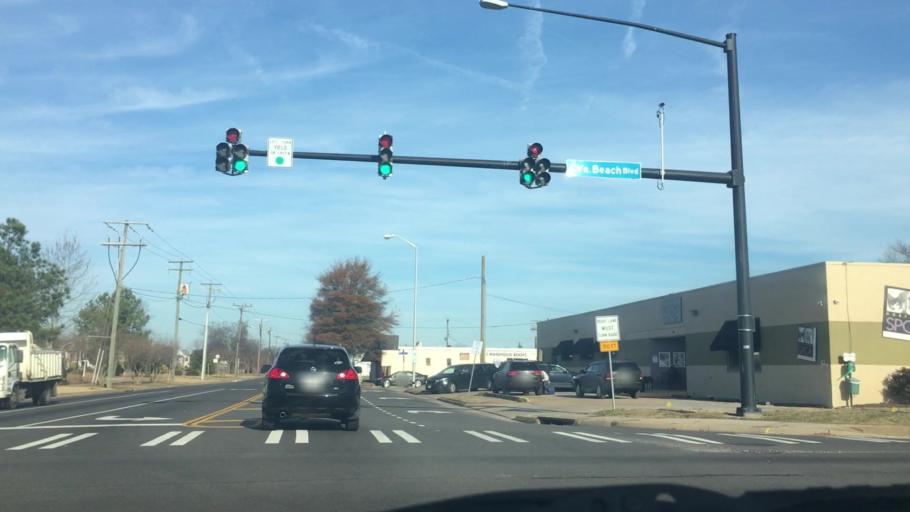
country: US
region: Virginia
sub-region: City of Norfolk
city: Norfolk
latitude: 36.8531
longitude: -76.2481
